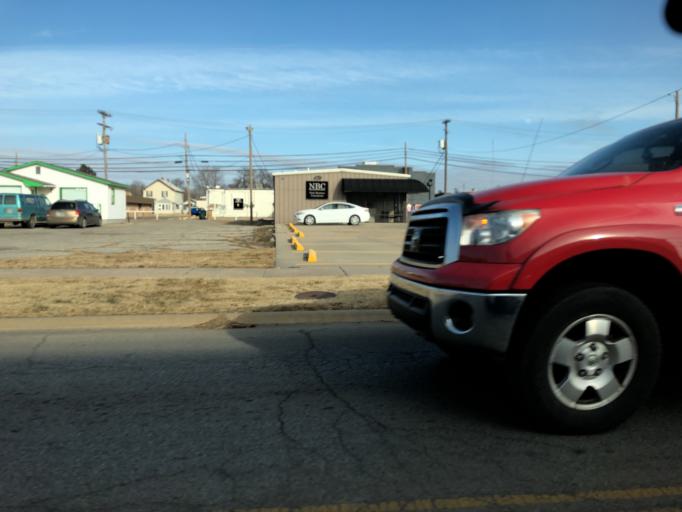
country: US
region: Kansas
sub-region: Reno County
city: Hutchinson
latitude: 38.0572
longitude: -97.9341
